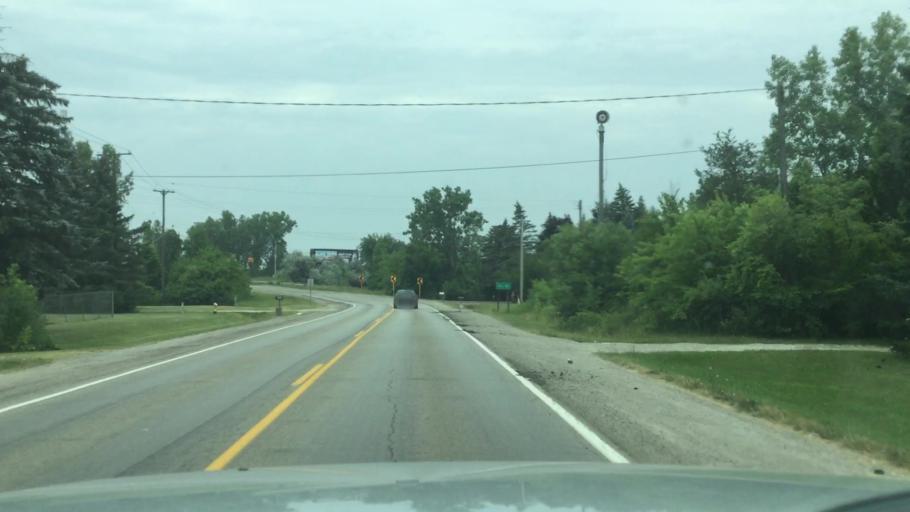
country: US
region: Michigan
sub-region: Genesee County
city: Flint
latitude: 42.9463
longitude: -83.7122
